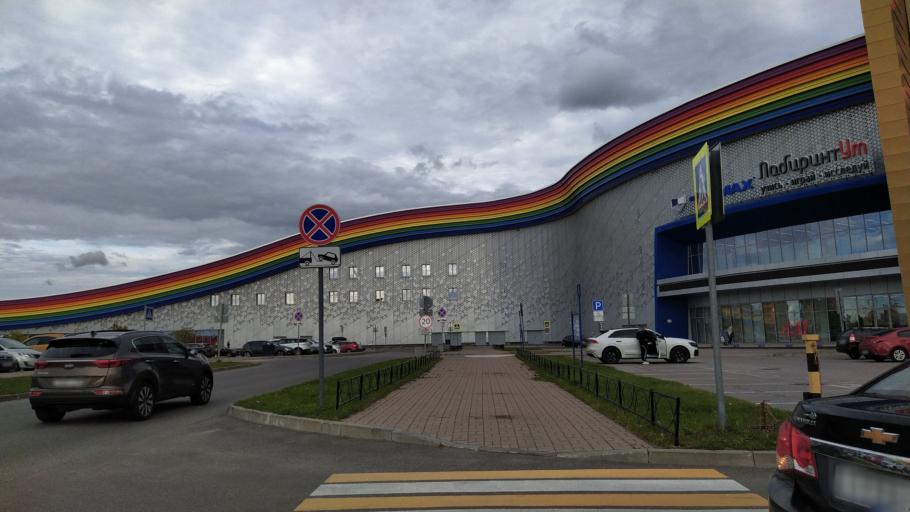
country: RU
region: St.-Petersburg
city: Kupchino
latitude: 59.8671
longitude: 30.3480
